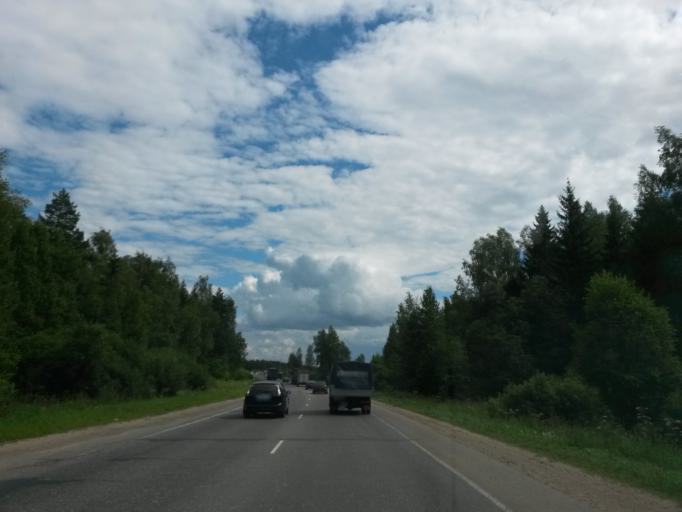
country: RU
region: Ivanovo
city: Novo-Talitsy
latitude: 57.0164
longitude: 40.7854
